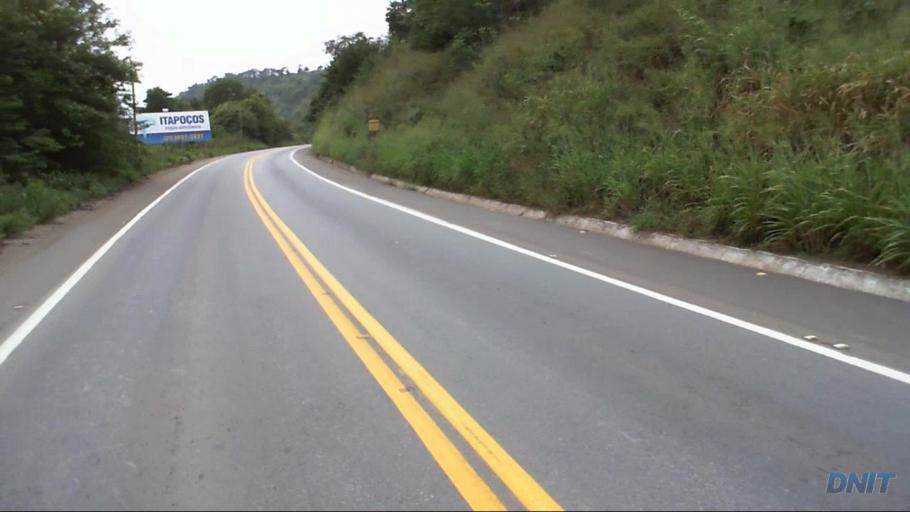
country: BR
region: Minas Gerais
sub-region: Timoteo
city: Timoteo
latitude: -19.5494
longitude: -42.7012
